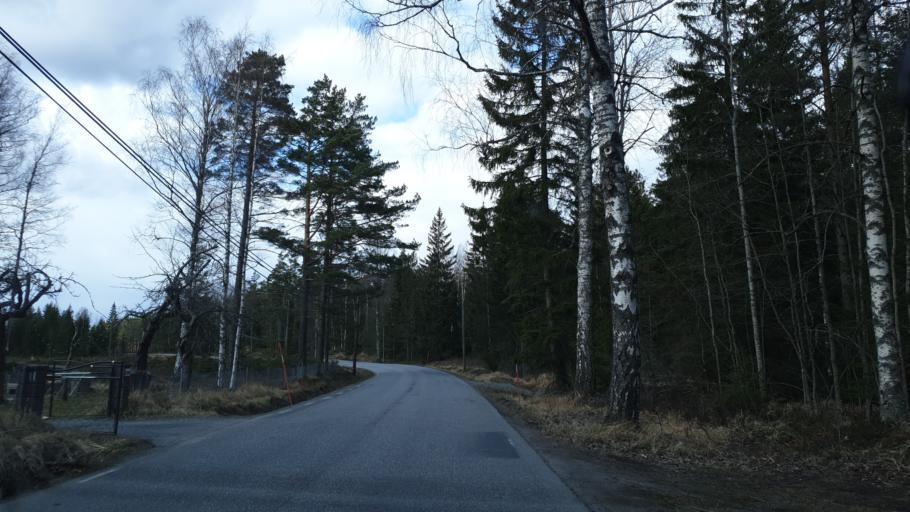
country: SE
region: Stockholm
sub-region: Tyreso Kommun
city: Brevik
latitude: 59.2484
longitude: 18.4408
